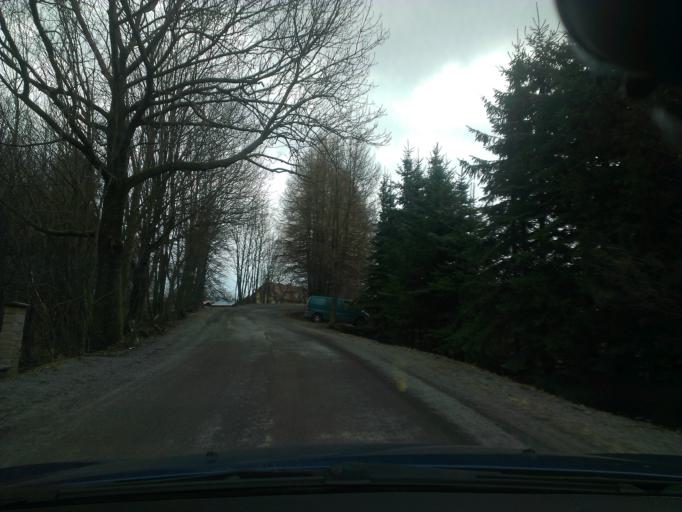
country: SK
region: Banskobystricky
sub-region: Okres Banska Bystrica
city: Banska Stiavnica
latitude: 48.4482
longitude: 18.8782
